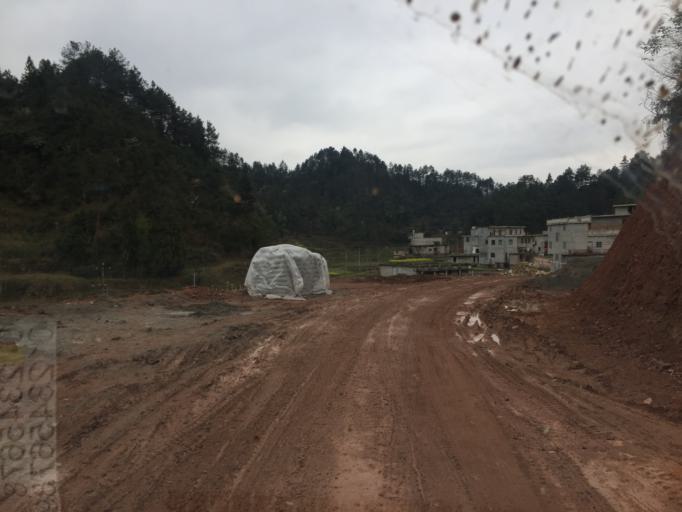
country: CN
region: Guizhou Sheng
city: Fuxing
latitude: 28.0635
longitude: 107.9122
